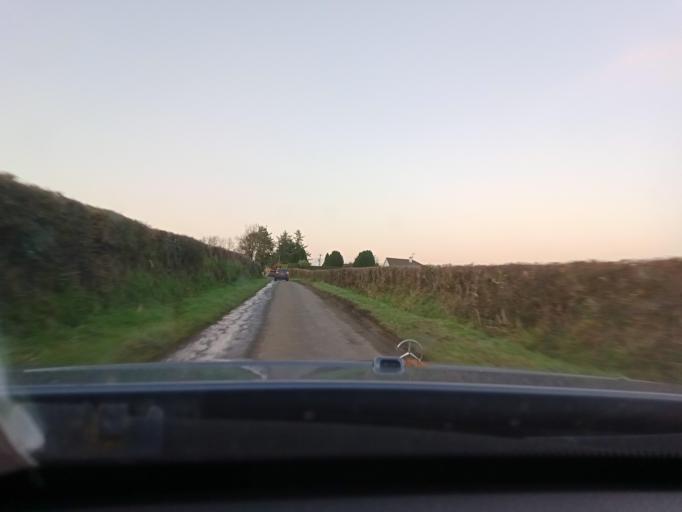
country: IE
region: Munster
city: Carrick-on-Suir
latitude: 52.4428
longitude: -7.3924
